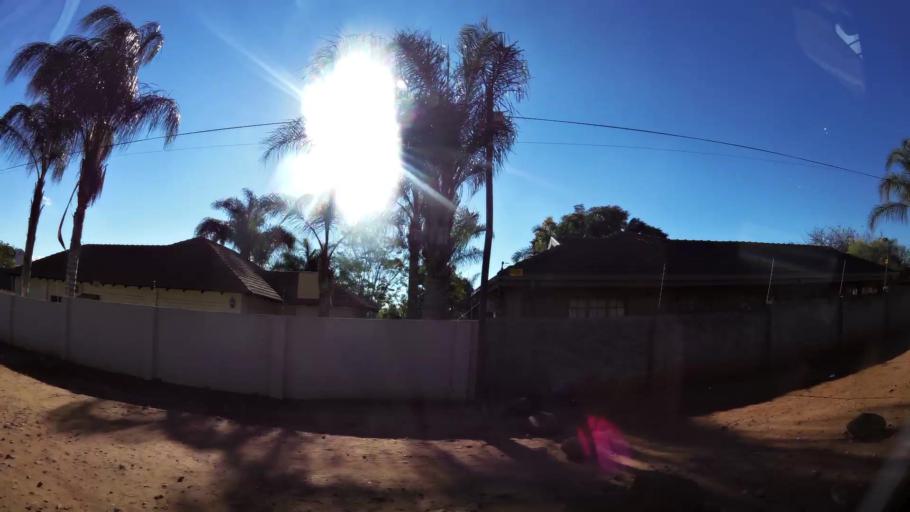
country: ZA
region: Limpopo
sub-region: Capricorn District Municipality
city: Polokwane
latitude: -23.8950
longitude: 29.4822
